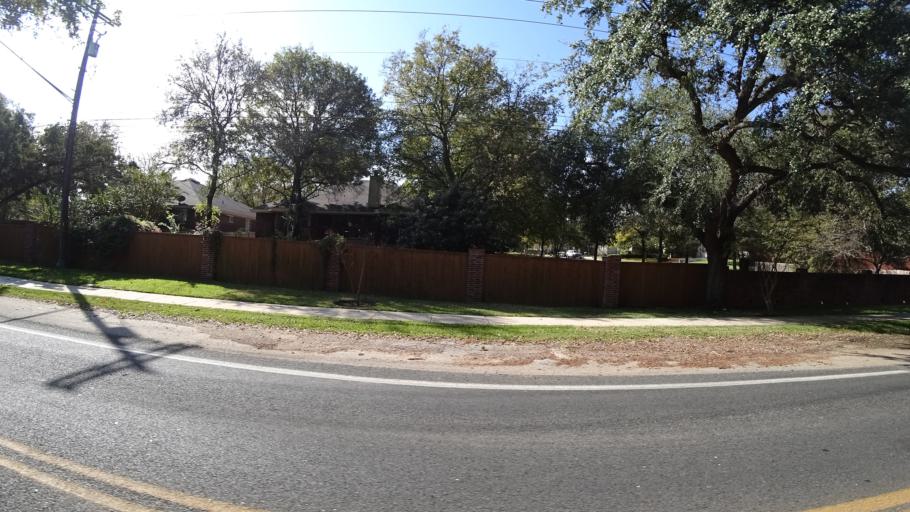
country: US
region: Texas
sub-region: Travis County
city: Shady Hollow
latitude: 30.1876
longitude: -97.8199
